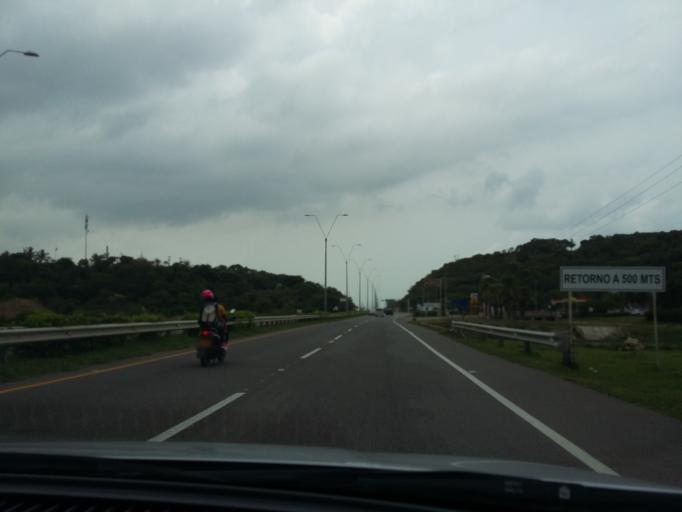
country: CO
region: Bolivar
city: Santa Rosa
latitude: 10.5173
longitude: -75.4684
